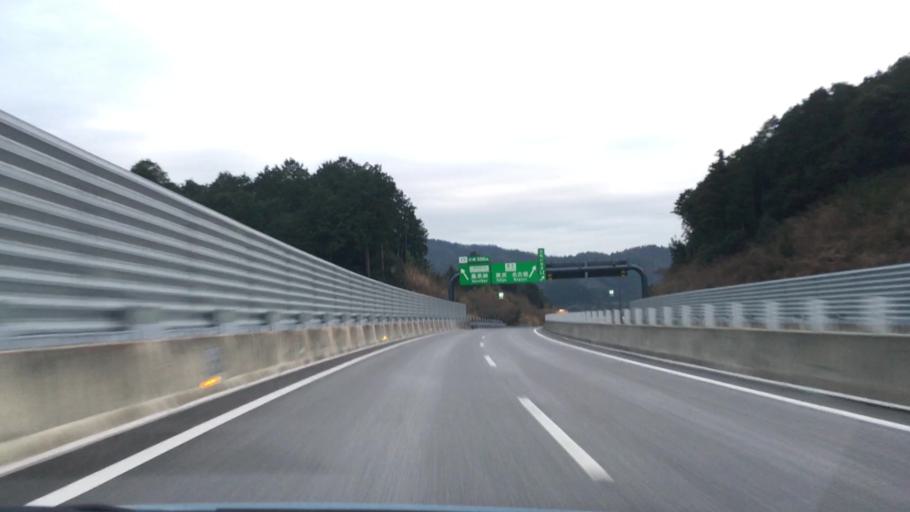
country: JP
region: Shizuoka
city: Hamakita
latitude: 34.8907
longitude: 137.6580
